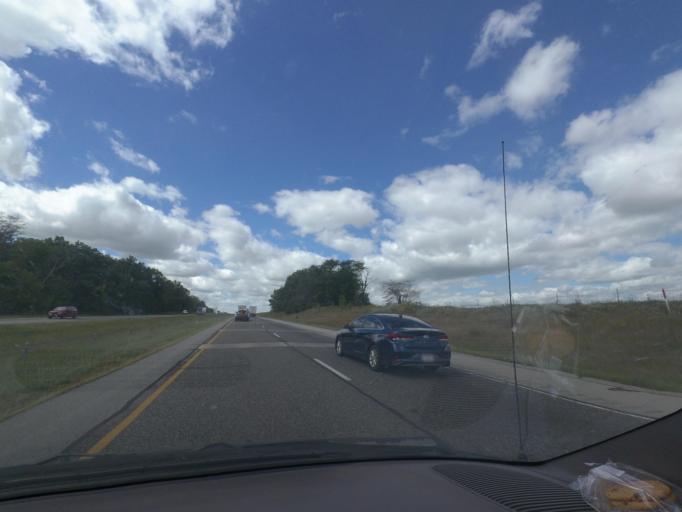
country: US
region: Indiana
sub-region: Wayne County
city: Centerville
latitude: 39.8541
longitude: -85.0815
